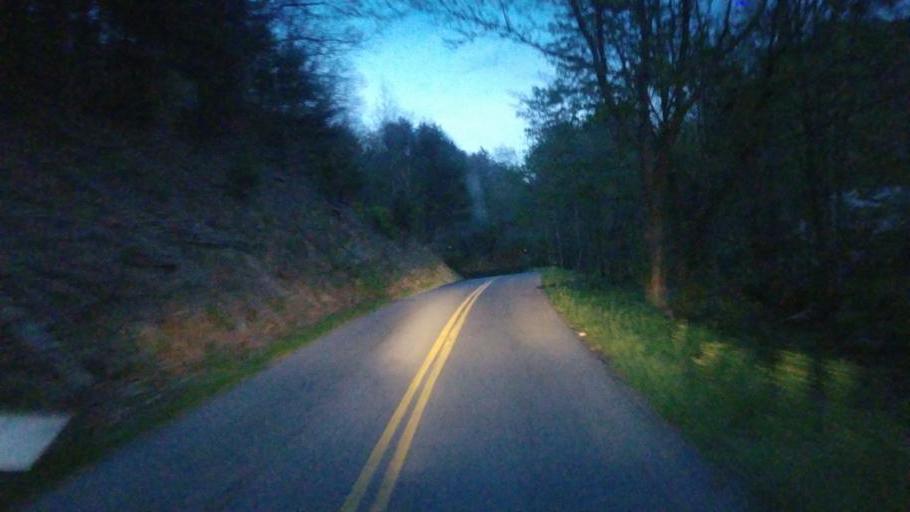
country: US
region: Virginia
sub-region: Smyth County
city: Atkins
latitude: 36.8410
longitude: -81.4584
